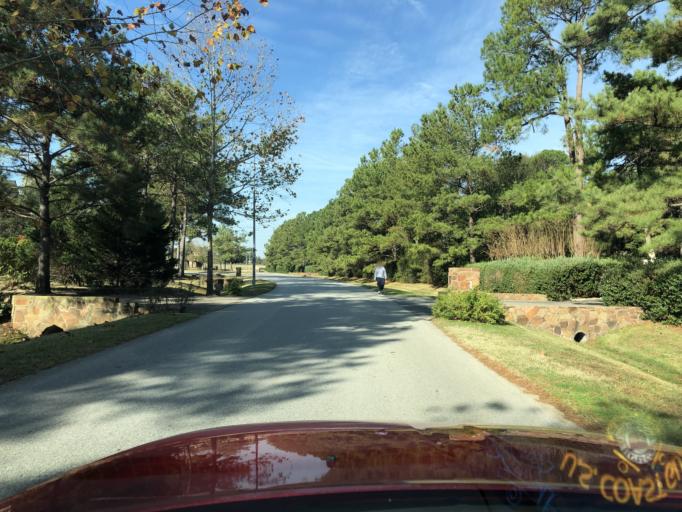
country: US
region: Texas
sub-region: Harris County
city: Tomball
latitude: 30.0399
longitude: -95.5610
